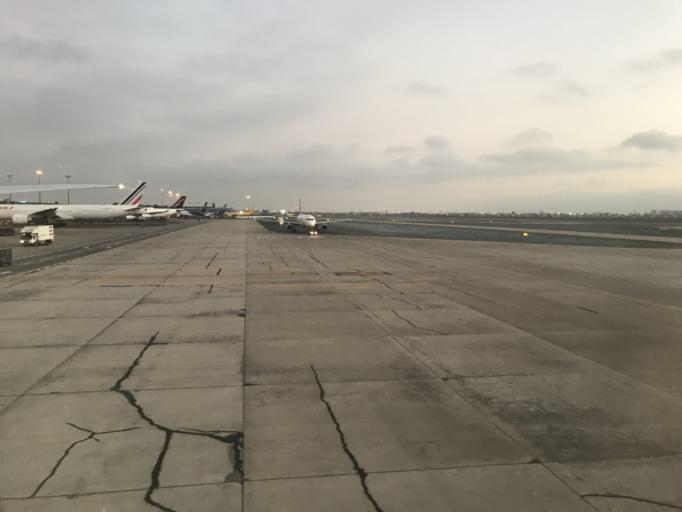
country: PE
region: Callao
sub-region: Callao
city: Callao
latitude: -12.0240
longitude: -77.1101
